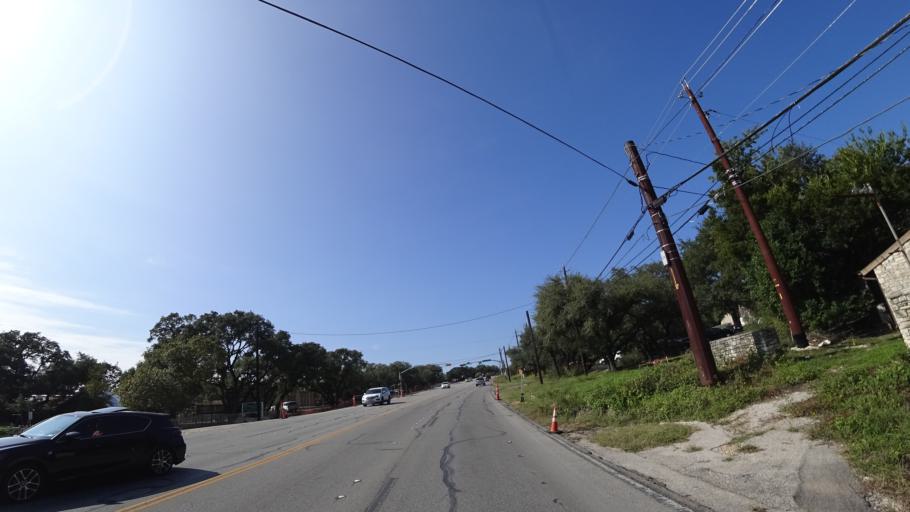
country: US
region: Texas
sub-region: Travis County
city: West Lake Hills
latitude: 30.2822
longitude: -97.8095
